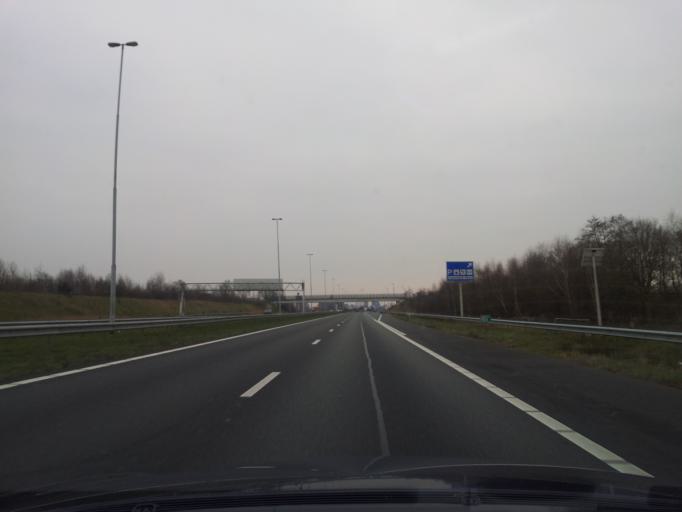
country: NL
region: North Brabant
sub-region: Gemeente Breda
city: Breda
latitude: 51.5080
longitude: 4.7440
